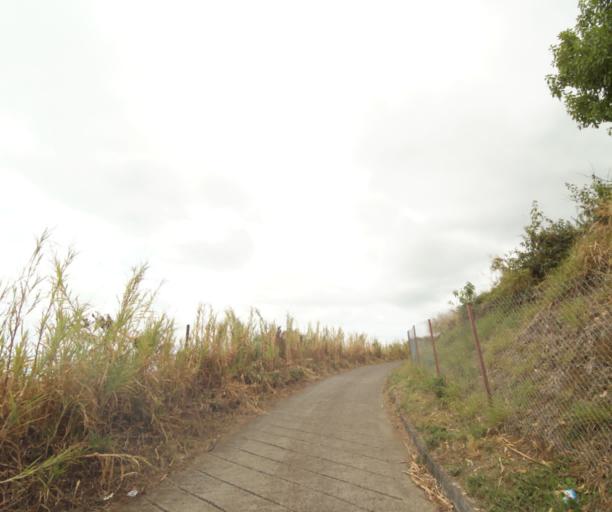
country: RE
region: Reunion
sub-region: Reunion
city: Saint-Paul
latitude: -21.0157
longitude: 55.3311
